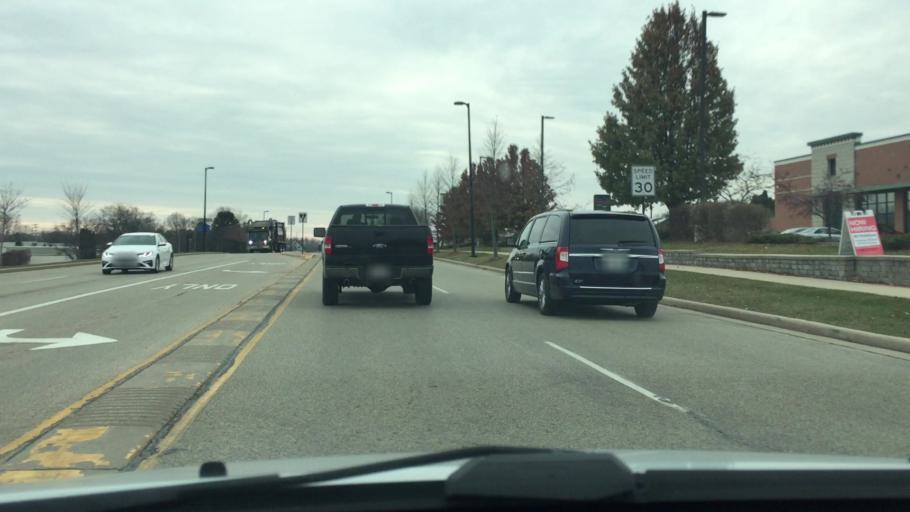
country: US
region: Wisconsin
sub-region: Ozaukee County
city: Grafton
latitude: 43.3085
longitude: -87.9585
